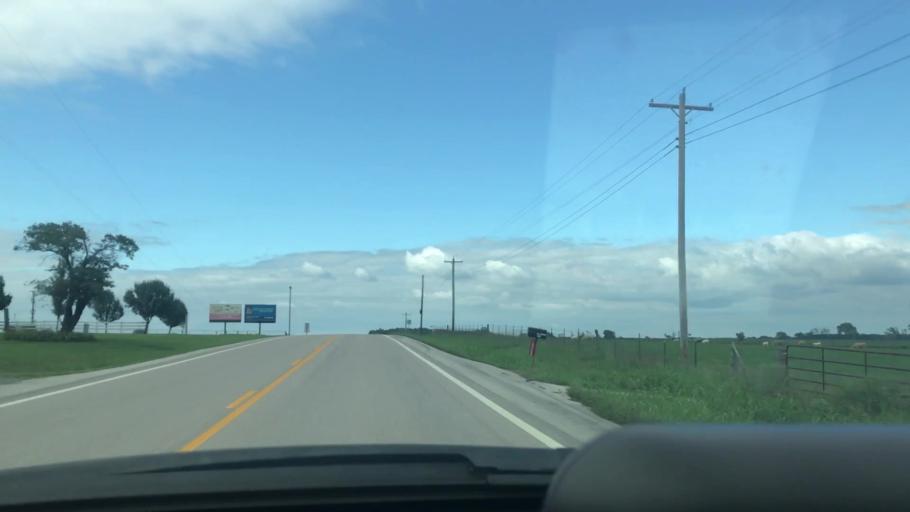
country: US
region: Missouri
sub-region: Hickory County
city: Hermitage
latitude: 37.9466
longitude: -93.2077
